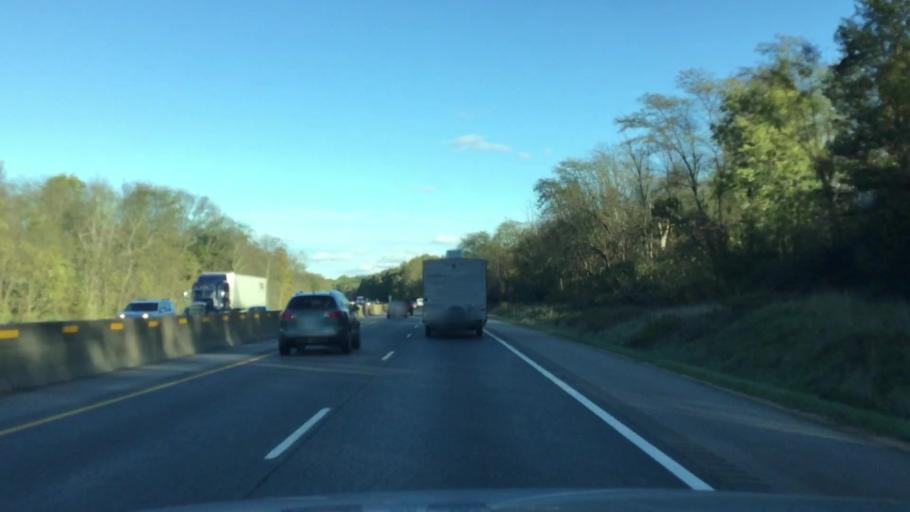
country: US
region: Michigan
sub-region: Kalamazoo County
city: Galesburg
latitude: 42.2693
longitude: -85.4600
